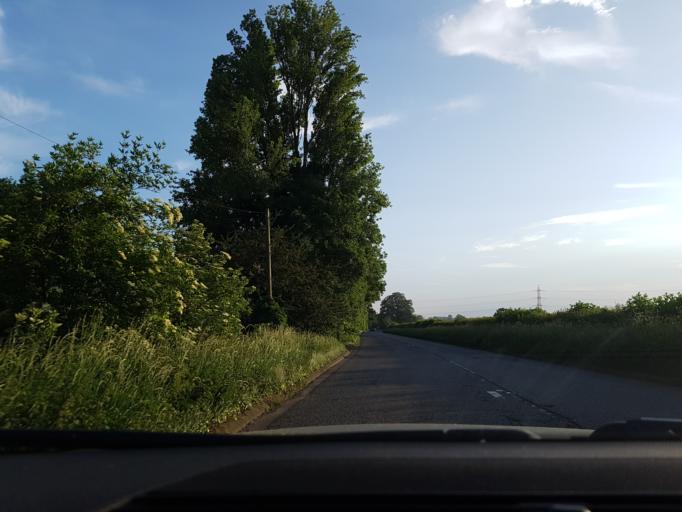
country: GB
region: England
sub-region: Buckinghamshire
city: Buckingham
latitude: 52.0144
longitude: -0.9414
